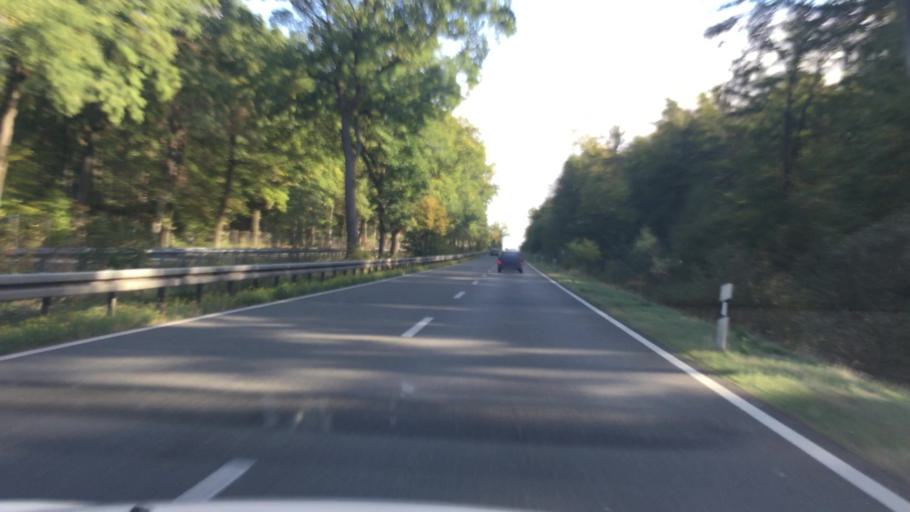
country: DE
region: Lower Saxony
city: Linsburg
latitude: 52.5698
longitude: 9.3137
